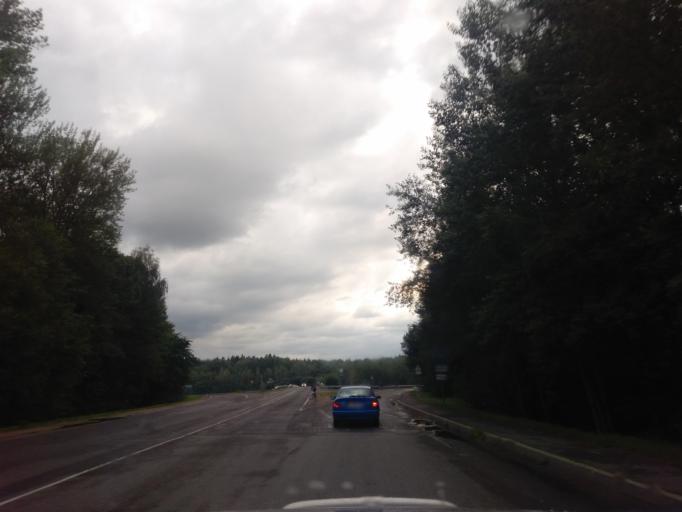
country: BY
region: Minsk
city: Enyerhyetykaw
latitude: 53.5898
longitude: 27.0438
